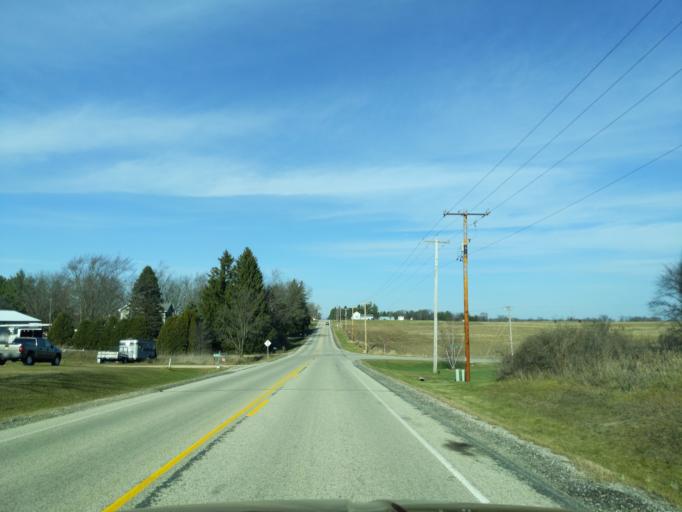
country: US
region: Wisconsin
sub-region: Walworth County
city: Elkhorn
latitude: 42.7599
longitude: -88.6030
